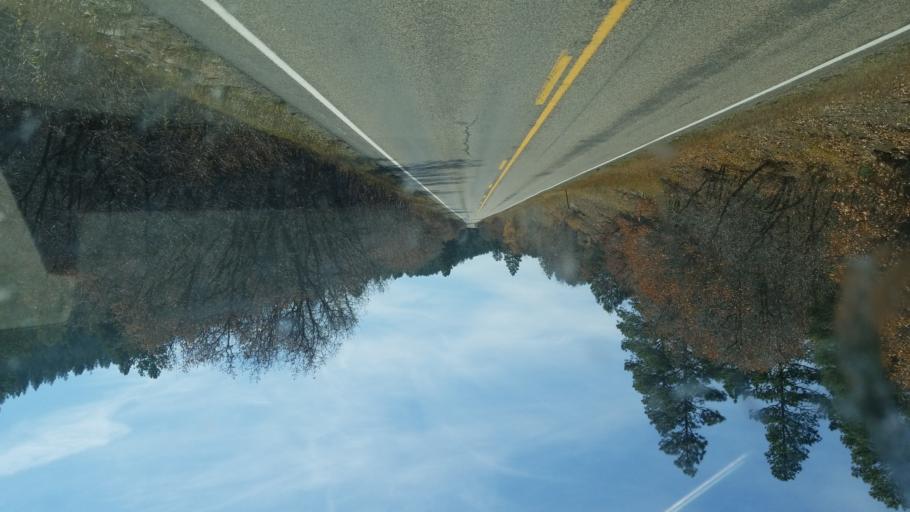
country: US
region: New Mexico
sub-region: Rio Arriba County
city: Dulce
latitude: 37.0779
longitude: -106.8551
